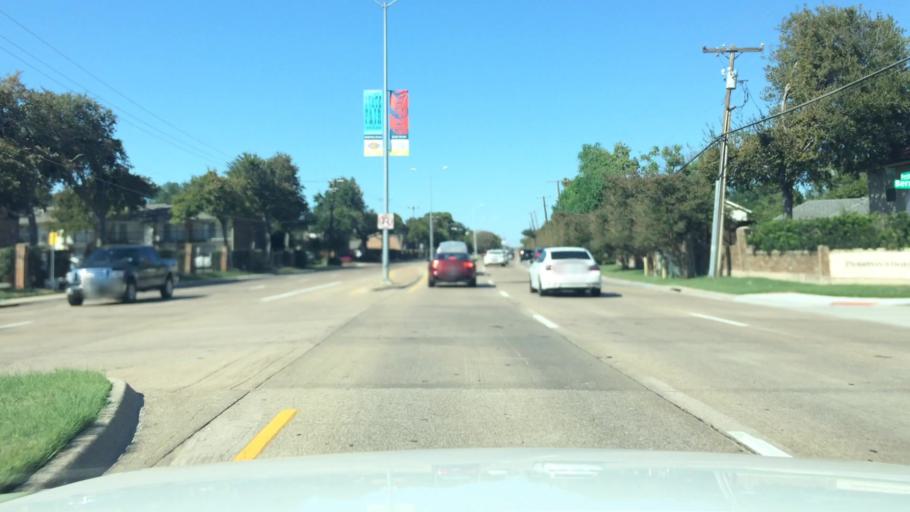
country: US
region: Texas
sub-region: Dallas County
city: Addison
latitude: 32.9560
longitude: -96.8045
